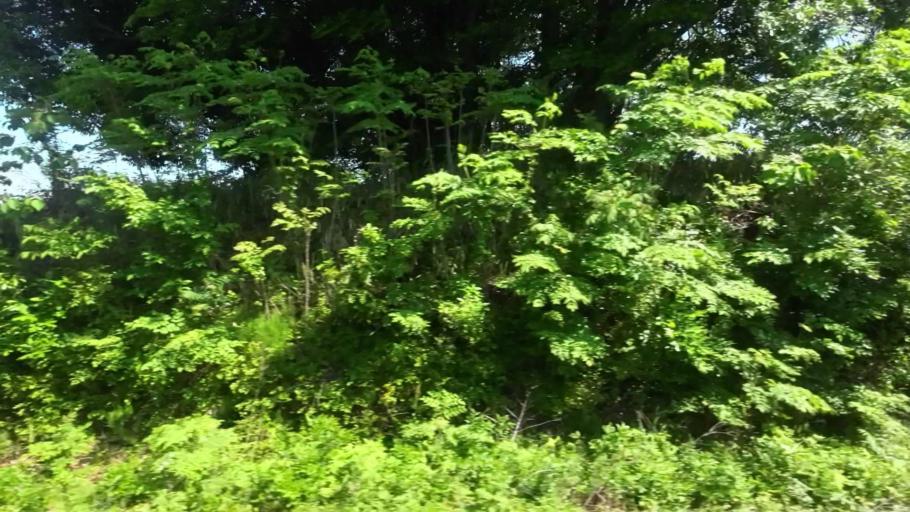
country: JP
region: Hiroshima
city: Fukuyama
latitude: 34.4657
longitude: 133.2942
